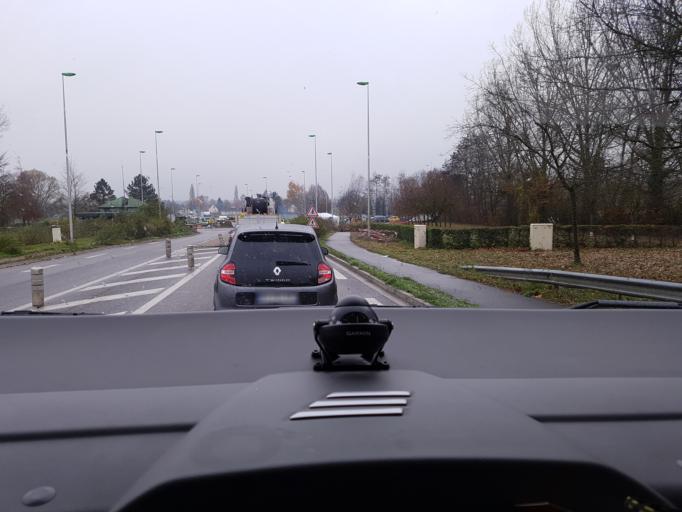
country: FR
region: Haute-Normandie
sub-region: Departement de la Seine-Maritime
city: Caudebec-en-Caux
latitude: 49.5115
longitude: 0.7413
